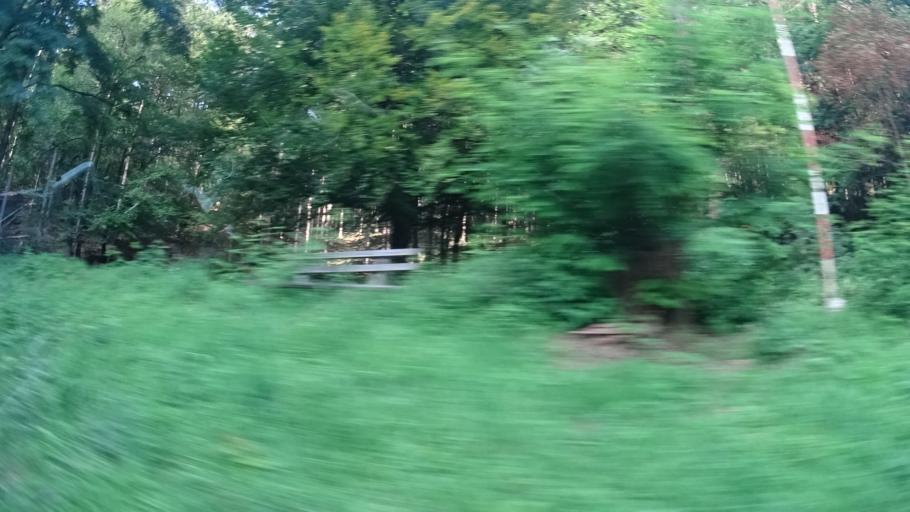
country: DE
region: Hesse
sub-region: Regierungsbezirk Darmstadt
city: Rothenberg
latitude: 49.5515
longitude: 8.9001
